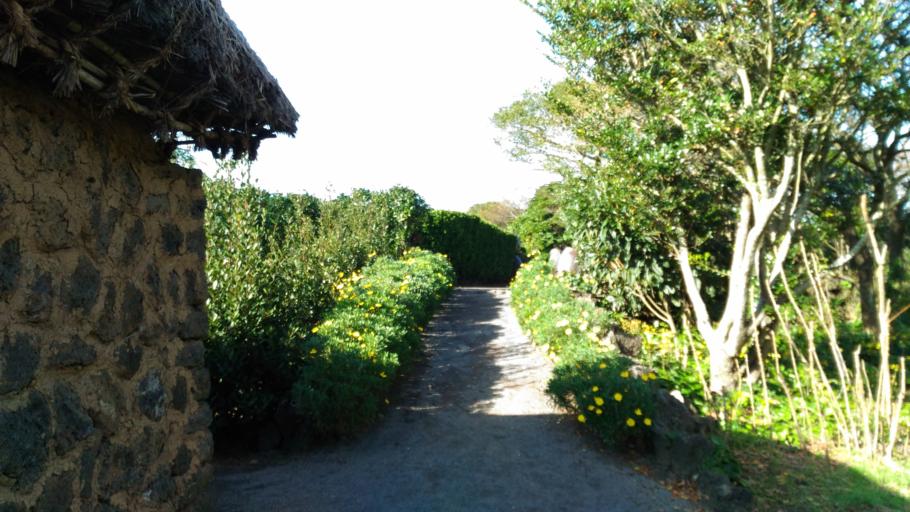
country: KR
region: Jeju-do
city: Seogwipo
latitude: 33.3224
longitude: 126.8401
